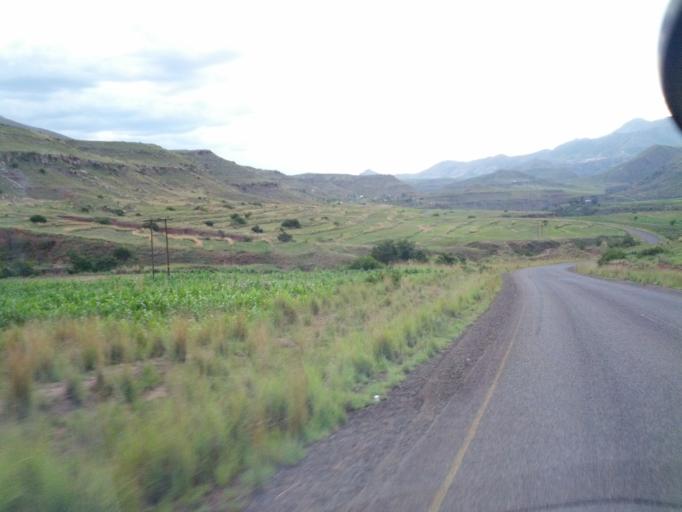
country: LS
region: Qacha's Nek
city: Qacha's Nek
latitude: -30.0689
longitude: 28.5577
